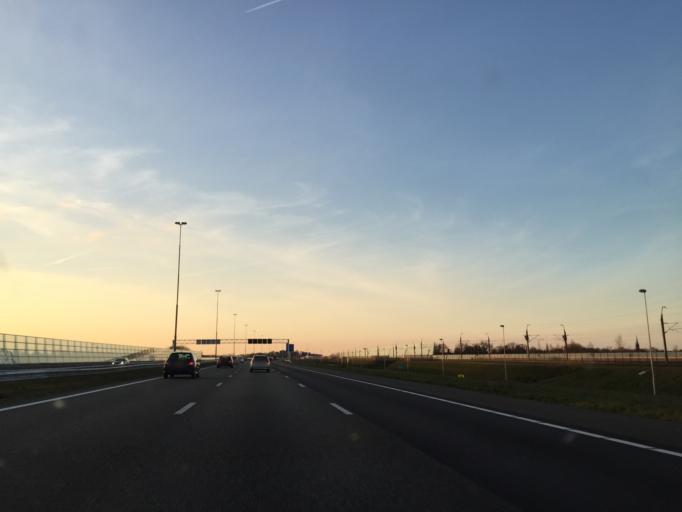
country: NL
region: North Brabant
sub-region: Gemeente Breda
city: Breda
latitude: 51.5613
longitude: 4.7345
